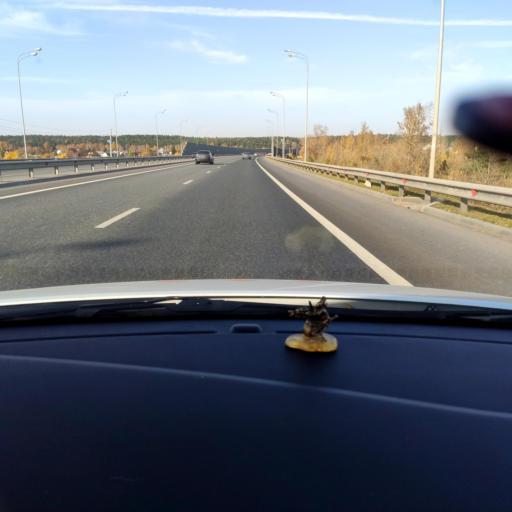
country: RU
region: Tatarstan
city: Osinovo
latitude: 55.8154
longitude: 48.8425
